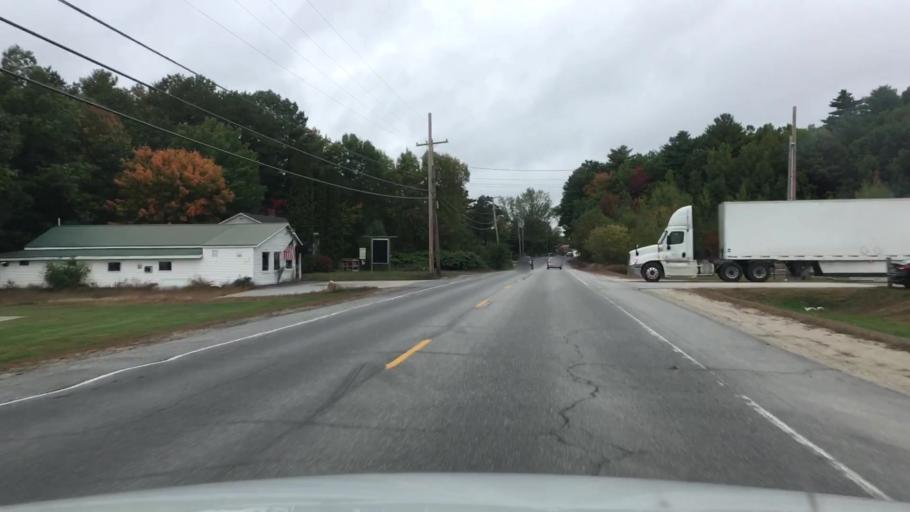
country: US
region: Maine
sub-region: Oxford County
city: Oxford
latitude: 44.1409
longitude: -70.4737
